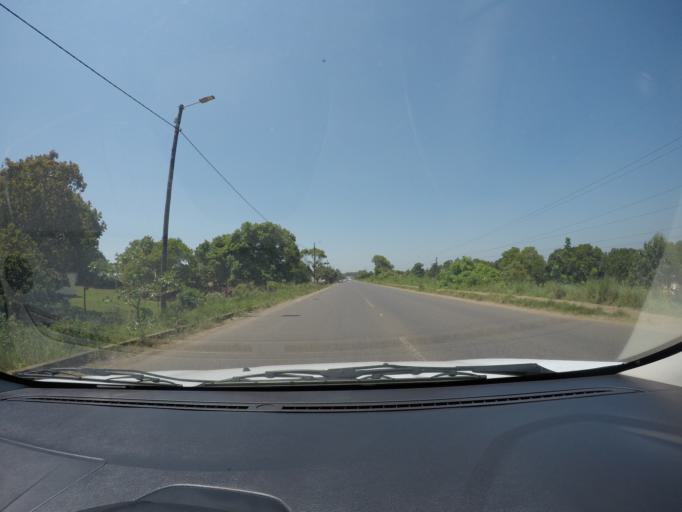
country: ZA
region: KwaZulu-Natal
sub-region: uThungulu District Municipality
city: eSikhawini
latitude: -28.8353
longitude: 31.9386
